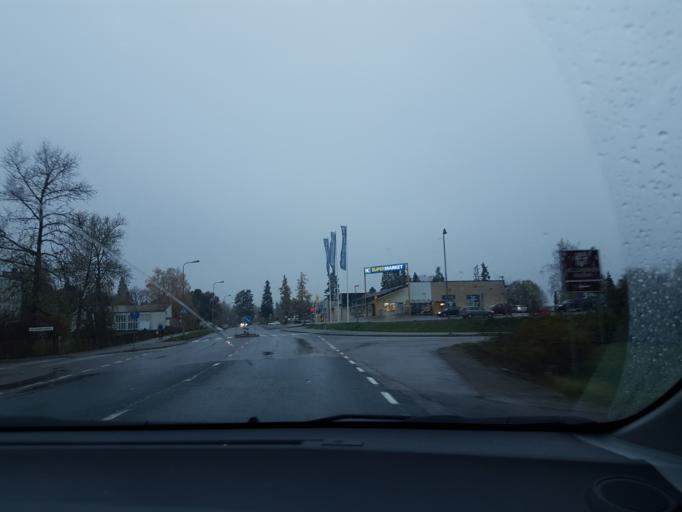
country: FI
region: Uusimaa
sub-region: Helsinki
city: Jaervenpaeae
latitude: 60.5303
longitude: 25.1083
